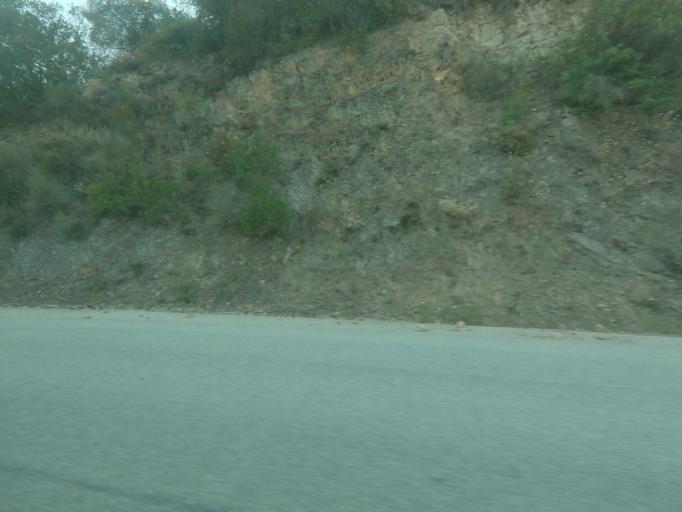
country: PT
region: Viseu
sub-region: Armamar
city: Armamar
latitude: 41.1096
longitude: -7.6786
